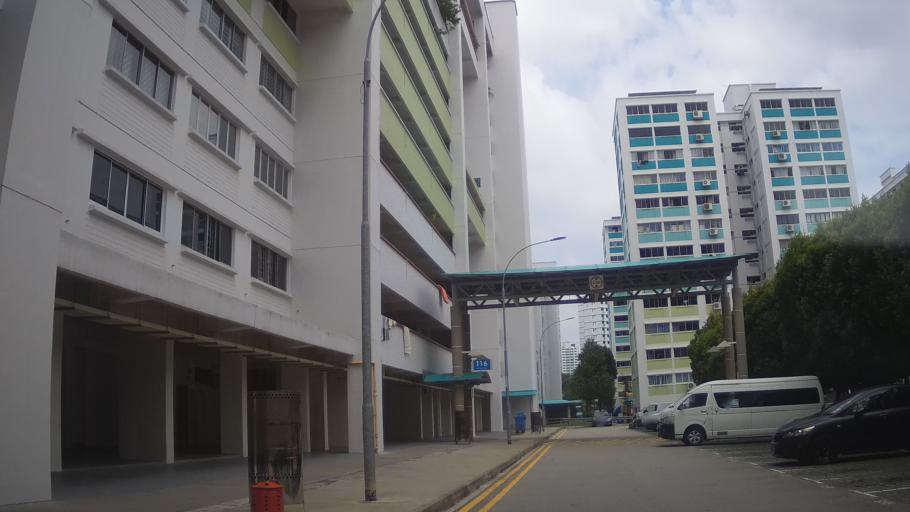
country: MY
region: Johor
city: Johor Bahru
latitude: 1.3771
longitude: 103.7689
